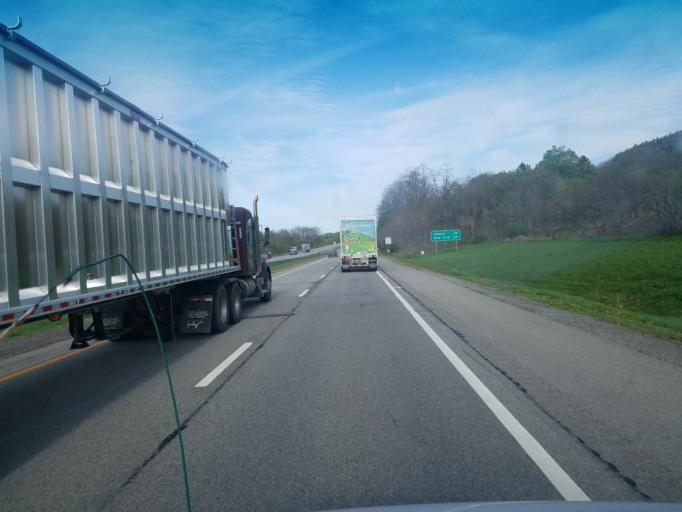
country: US
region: New York
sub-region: Herkimer County
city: Herkimer
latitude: 43.0137
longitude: -74.9323
